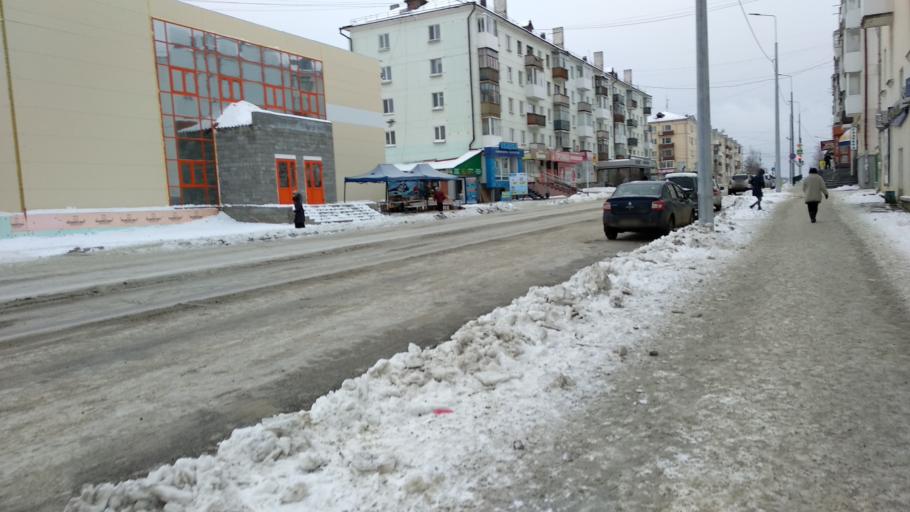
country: RU
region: Sverdlovsk
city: Krasnotur'insk
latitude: 59.7630
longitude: 60.2035
